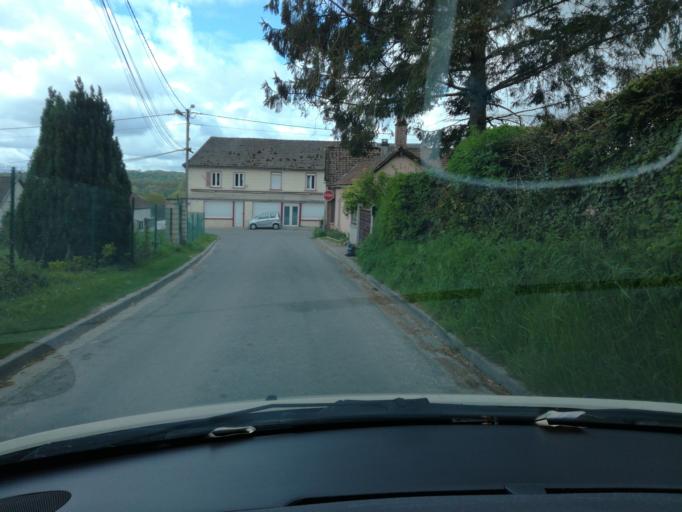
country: FR
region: Picardie
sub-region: Departement de la Somme
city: Pont-Remy
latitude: 50.0660
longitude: 1.8853
